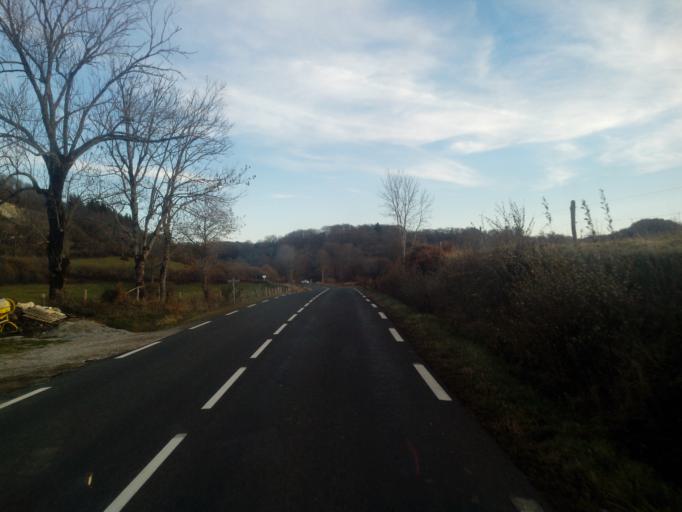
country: FR
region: Auvergne
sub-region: Departement du Cantal
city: Riom-es-Montagnes
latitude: 45.3125
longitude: 2.5970
